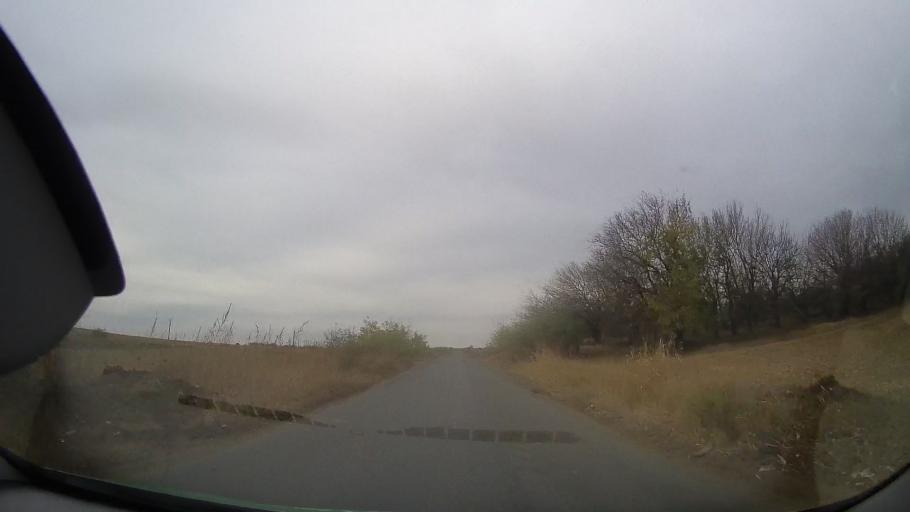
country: RO
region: Buzau
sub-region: Comuna Largu
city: Largu
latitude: 44.9729
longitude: 27.1680
